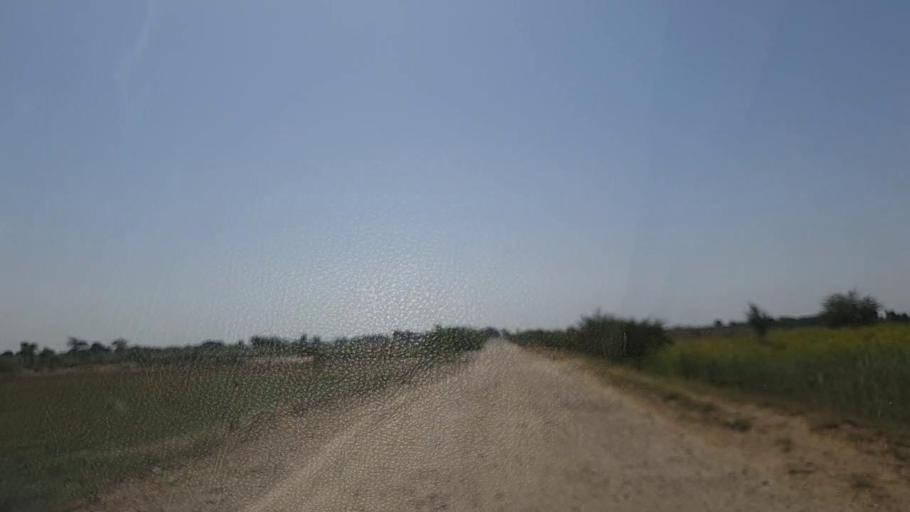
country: PK
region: Sindh
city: Samaro
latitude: 25.2212
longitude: 69.4042
